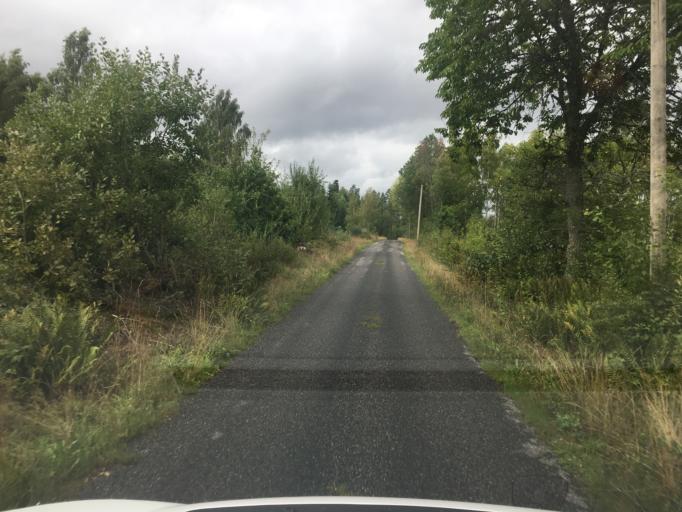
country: SE
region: Kronoberg
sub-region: Ljungby Kommun
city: Lagan
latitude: 56.9354
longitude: 14.0251
